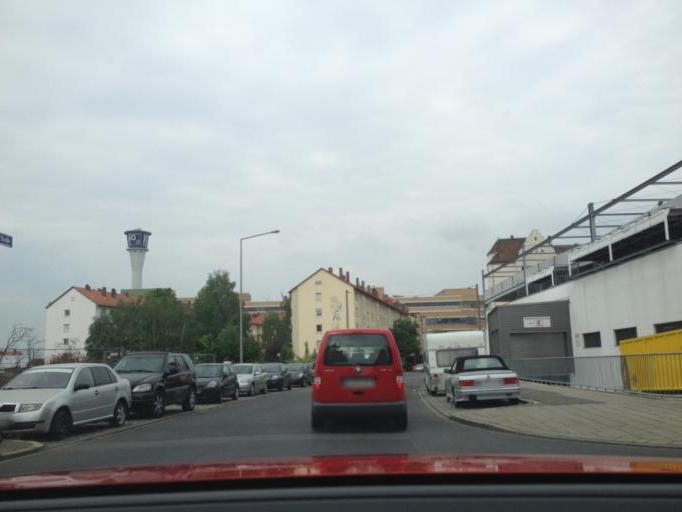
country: DE
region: Bavaria
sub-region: Regierungsbezirk Mittelfranken
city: Wetzendorf
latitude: 49.4555
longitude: 11.0365
